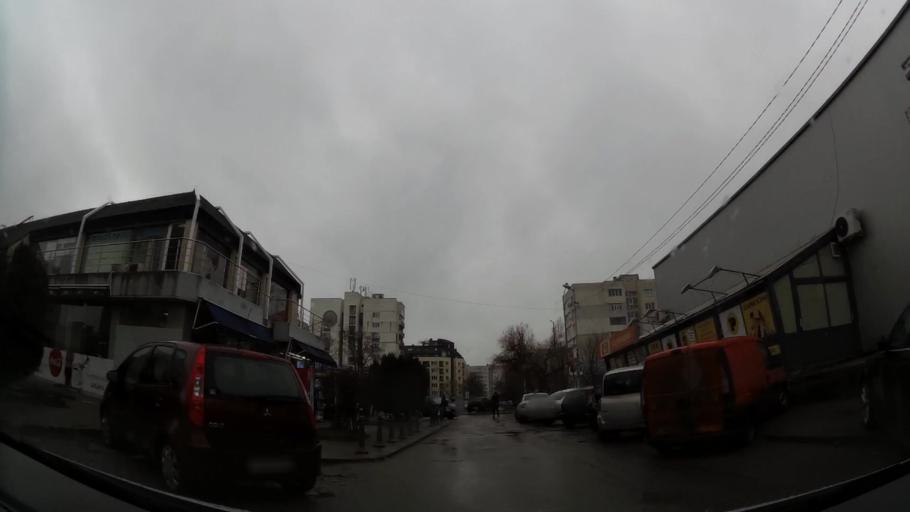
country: BG
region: Sofia-Capital
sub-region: Stolichna Obshtina
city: Sofia
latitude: 42.6358
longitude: 23.3776
